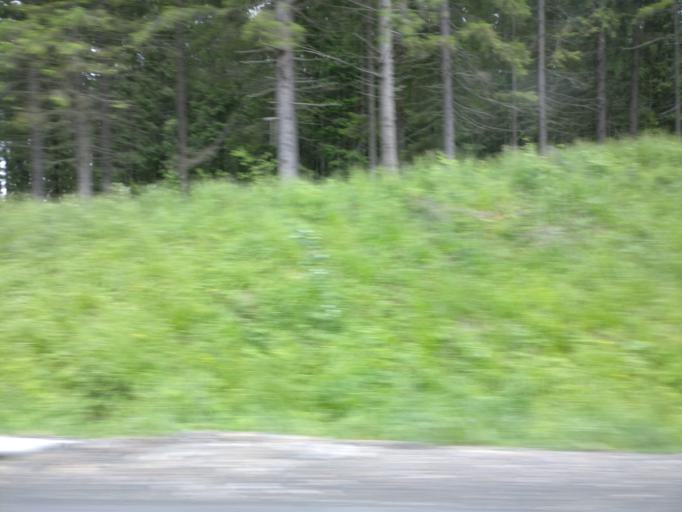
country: FI
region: Northern Savo
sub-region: Varkaus
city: Leppaevirta
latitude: 62.6061
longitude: 27.6217
